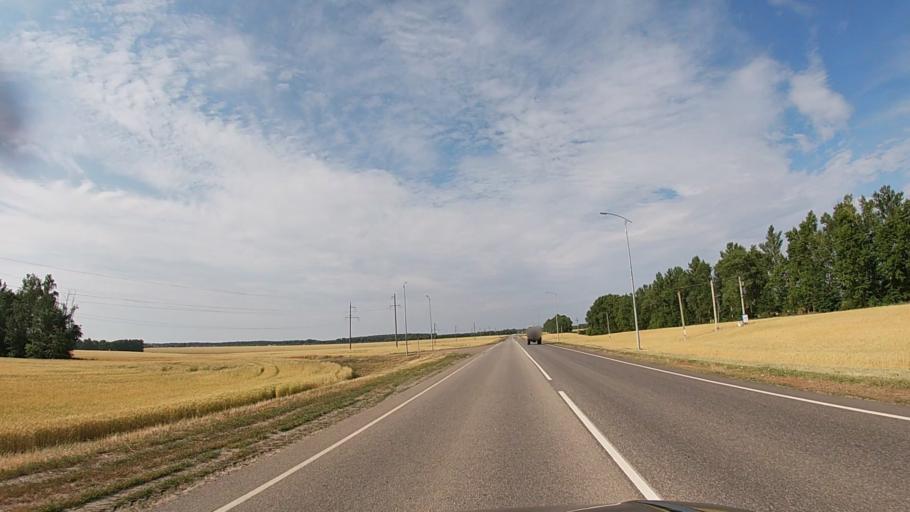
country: RU
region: Belgorod
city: Proletarskiy
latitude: 50.8138
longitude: 35.7502
